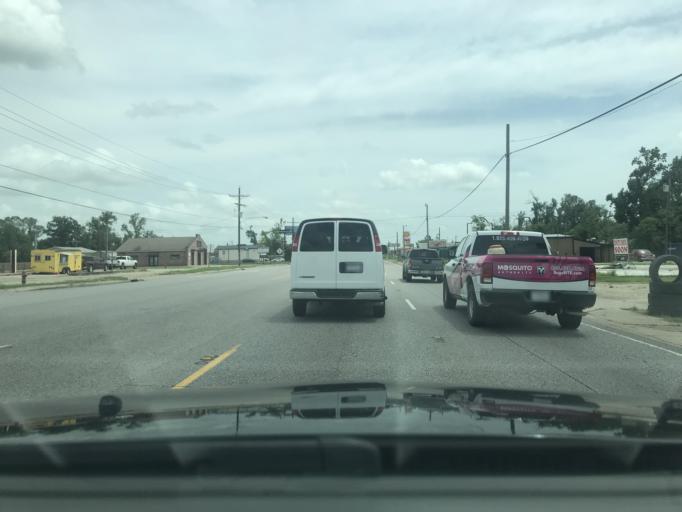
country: US
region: Louisiana
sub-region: Calcasieu Parish
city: Moss Bluff
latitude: 30.2599
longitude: -93.1806
